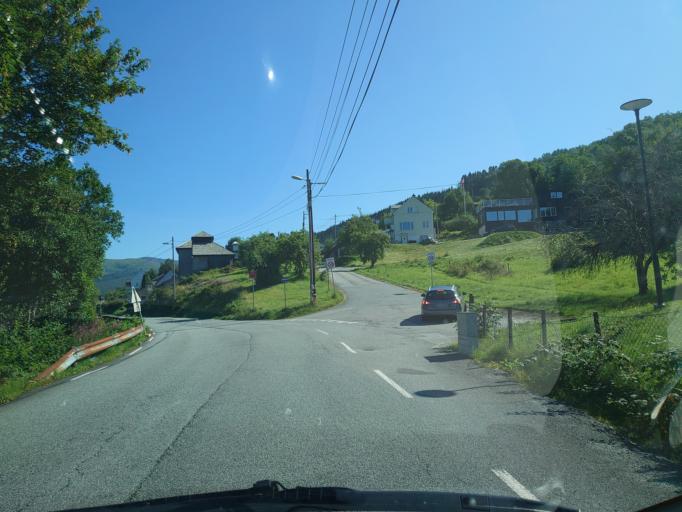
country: NO
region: Hordaland
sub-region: Bergen
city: Indre Arna
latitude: 60.4423
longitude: 5.4760
